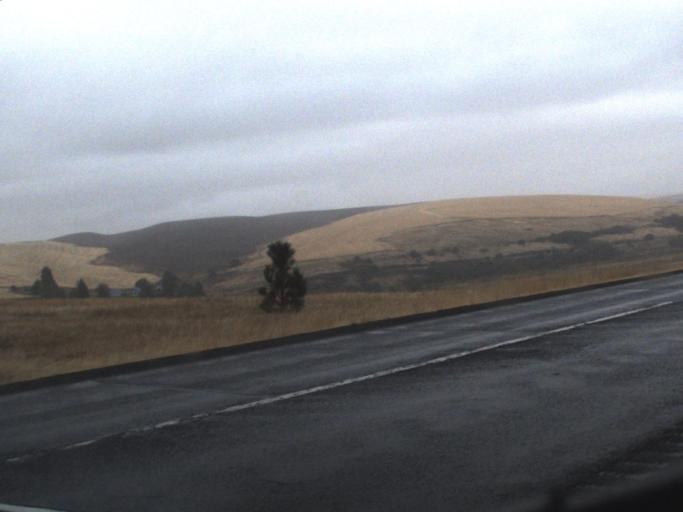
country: US
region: Washington
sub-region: Spokane County
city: Cheney
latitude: 47.2446
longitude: -117.3627
